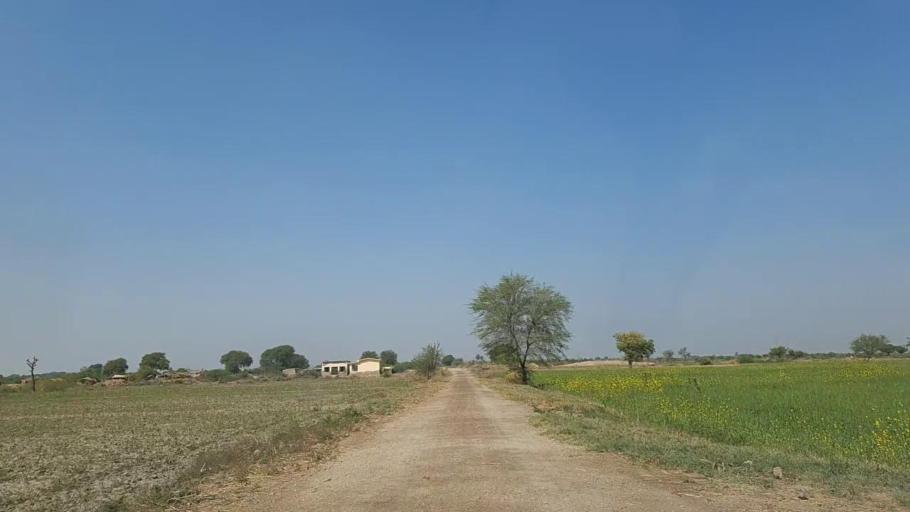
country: PK
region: Sindh
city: Digri
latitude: 25.2061
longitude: 69.1443
